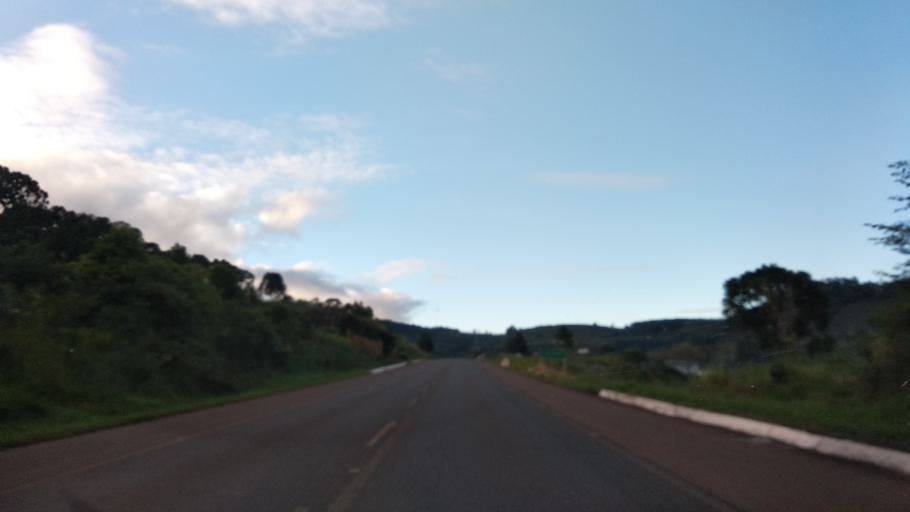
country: BR
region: Santa Catarina
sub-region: Curitibanos
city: Curitibanos
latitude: -27.5552
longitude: -50.8436
